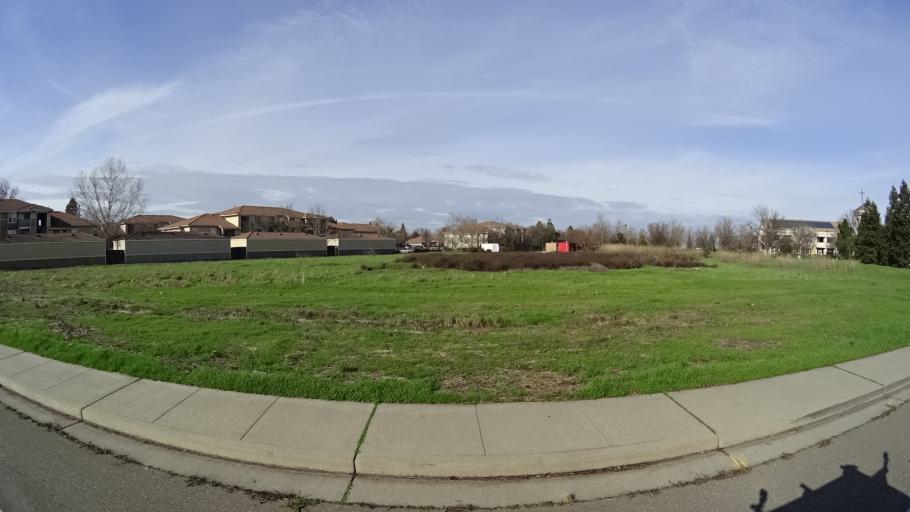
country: US
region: California
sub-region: Yolo County
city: Davis
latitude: 38.5564
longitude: -121.6957
